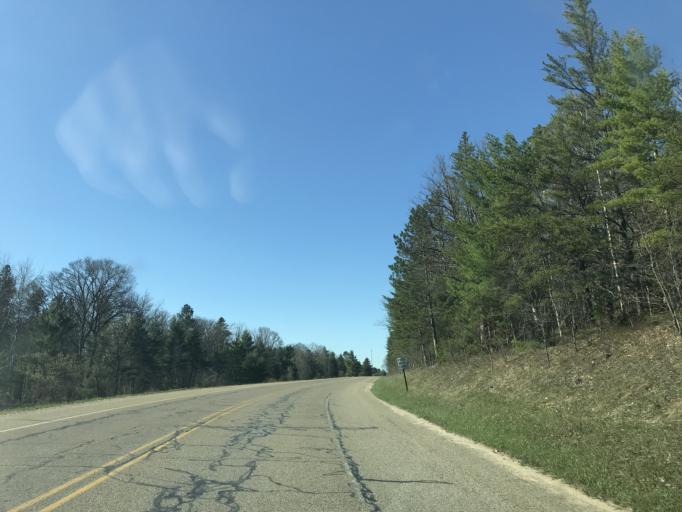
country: US
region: Michigan
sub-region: Crawford County
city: Grayling
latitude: 44.7224
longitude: -84.7470
